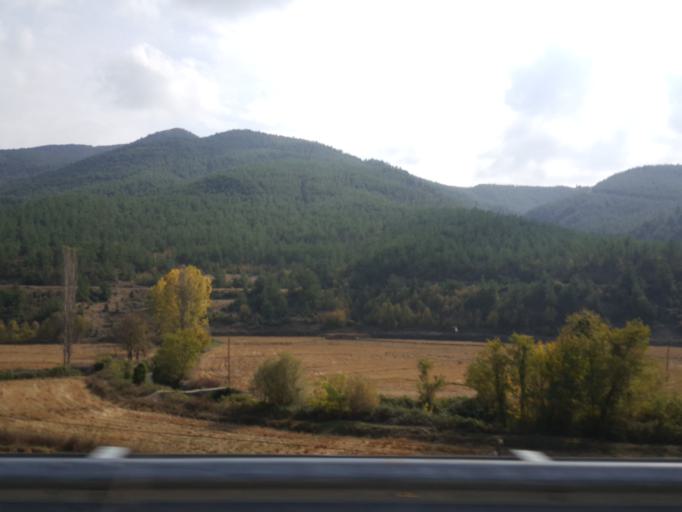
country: TR
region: Sinop
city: Sarayduzu
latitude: 41.3859
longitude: 34.9345
